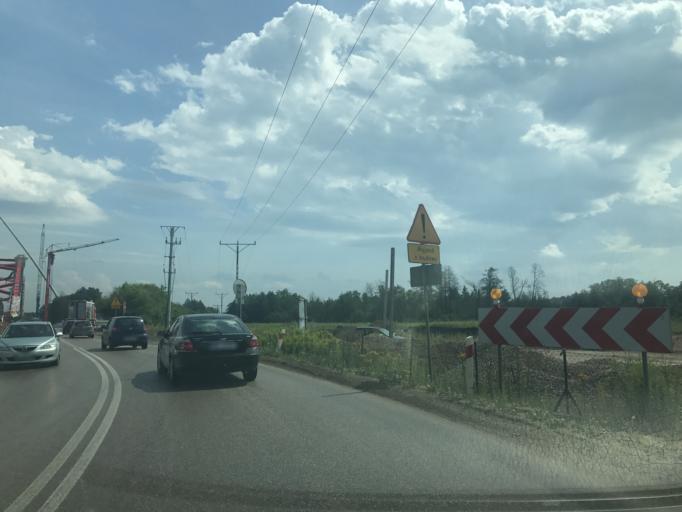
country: PL
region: Warmian-Masurian Voivodeship
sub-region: Powiat ostrodzki
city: Ostroda
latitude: 53.7146
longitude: 19.9603
